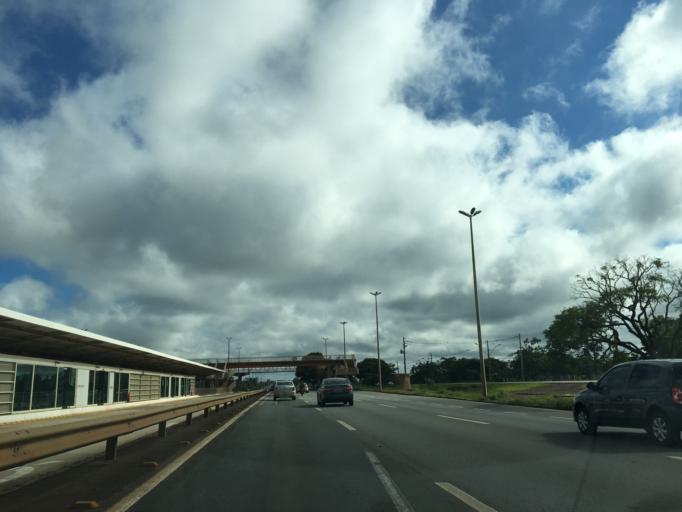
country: BR
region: Federal District
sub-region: Brasilia
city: Brasilia
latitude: -15.9238
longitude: -47.9758
